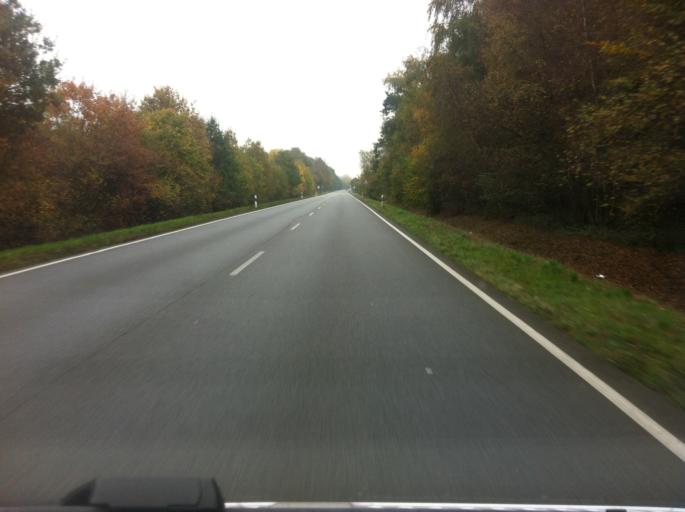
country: DE
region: North Rhine-Westphalia
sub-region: Regierungsbezirk Munster
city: Gescher
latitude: 51.9387
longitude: 6.9712
